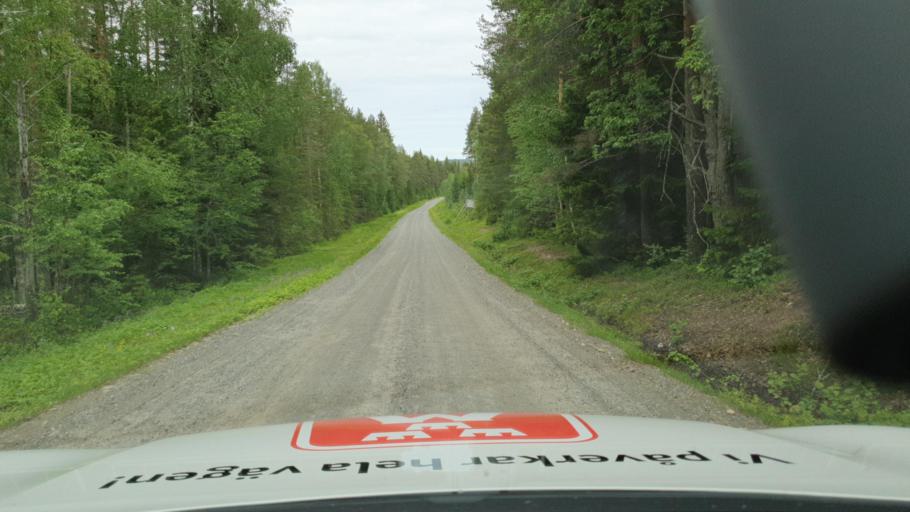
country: SE
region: Vaesterbotten
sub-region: Skelleftea Kommun
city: Burtraesk
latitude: 64.4422
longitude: 20.3664
